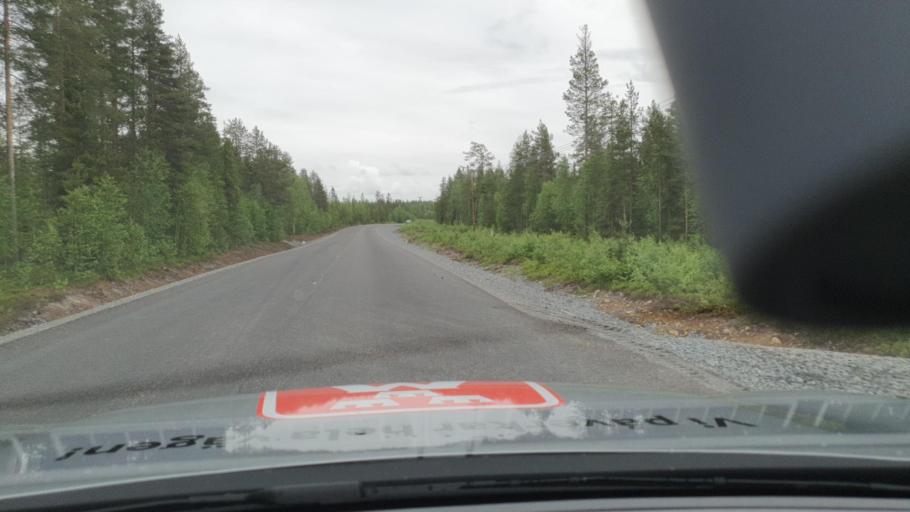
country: SE
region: Norrbotten
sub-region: Overtornea Kommun
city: OEvertornea
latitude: 66.6321
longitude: 23.2657
